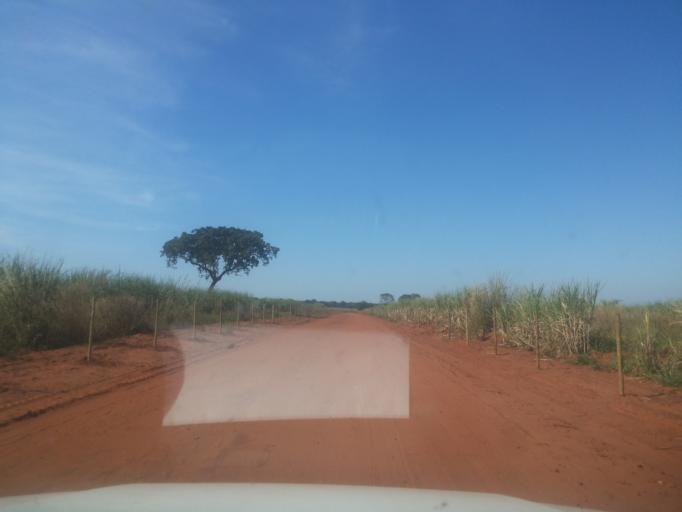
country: BR
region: Minas Gerais
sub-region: Santa Vitoria
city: Santa Vitoria
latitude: -19.0206
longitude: -50.3680
